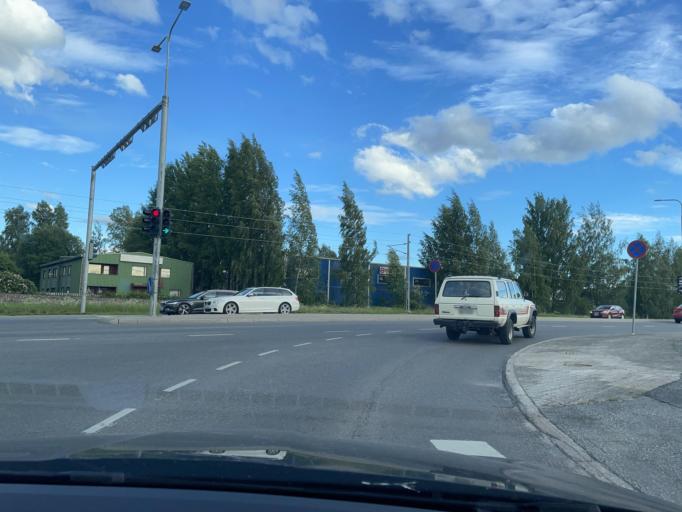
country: FI
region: Central Finland
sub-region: Jyvaeskylae
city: Jyvaeskylae
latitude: 62.2541
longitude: 25.7769
